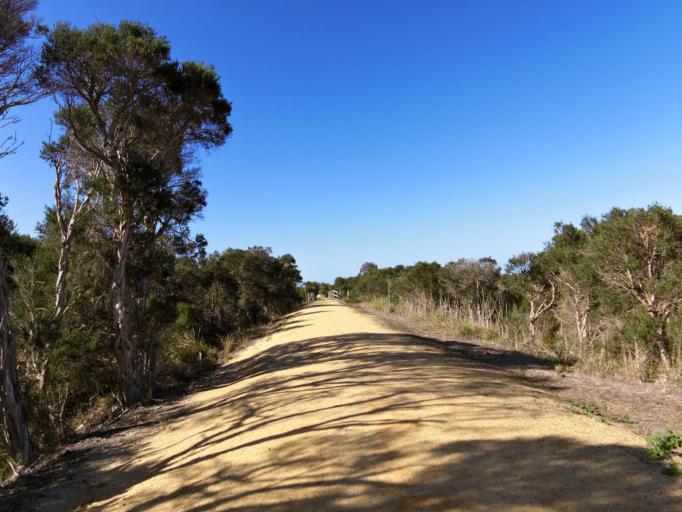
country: AU
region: Victoria
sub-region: Bass Coast
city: North Wonthaggi
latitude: -38.5794
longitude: 145.5518
